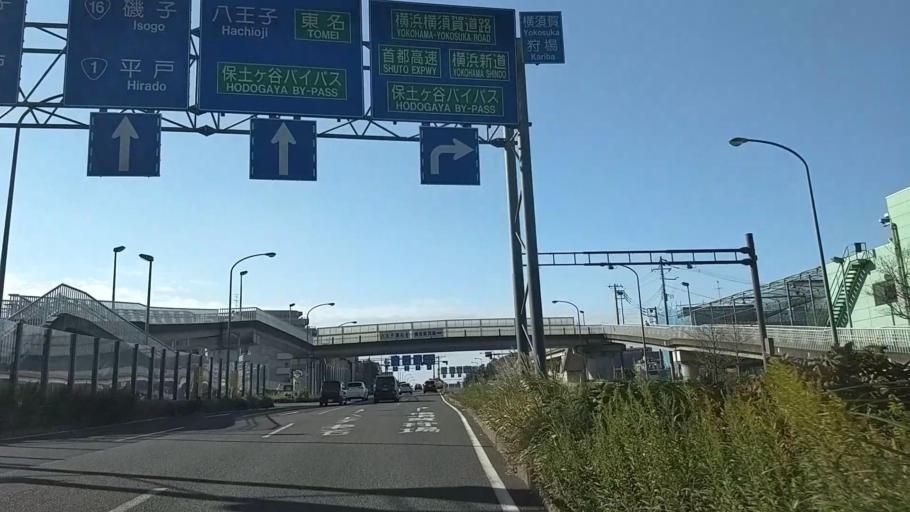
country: JP
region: Kanagawa
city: Yokohama
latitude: 35.4546
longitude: 139.5629
